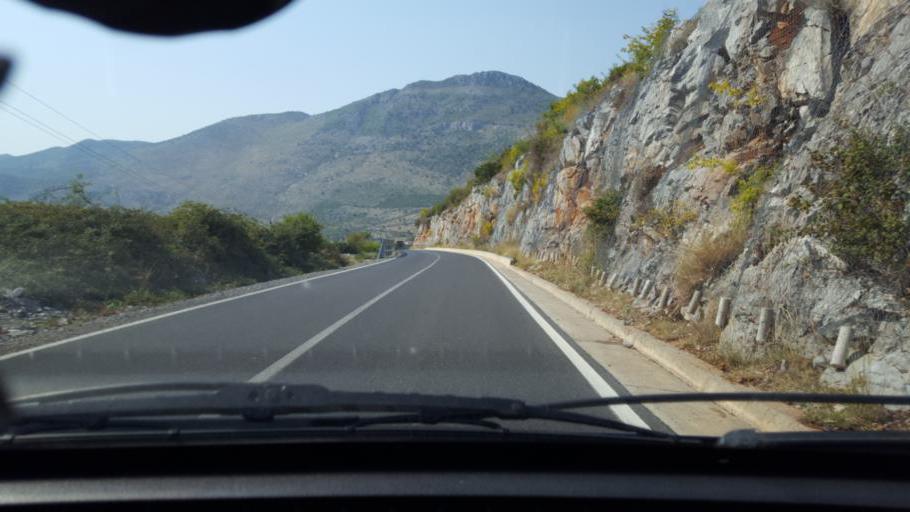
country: AL
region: Shkoder
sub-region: Rrethi i Malesia e Madhe
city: Hot
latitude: 42.3742
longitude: 19.4600
